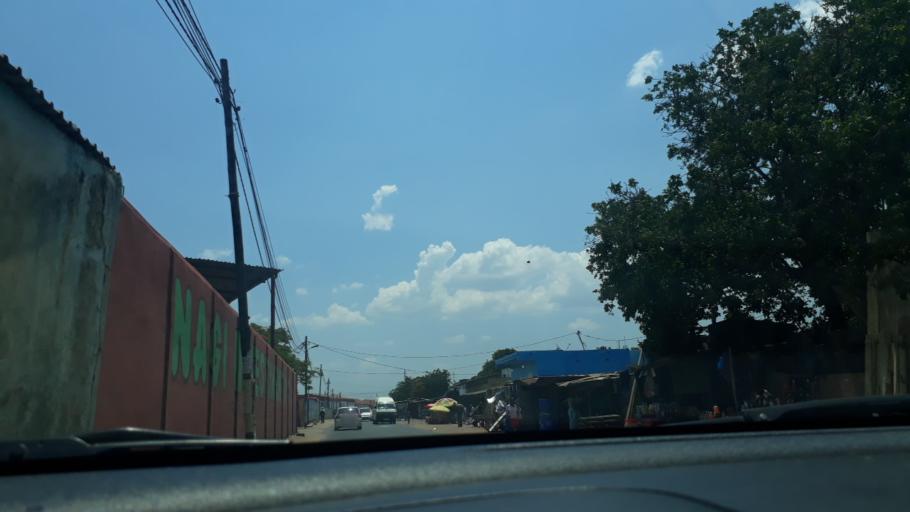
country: MZ
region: Maputo City
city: Maputo
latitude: -25.9348
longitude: 32.5577
